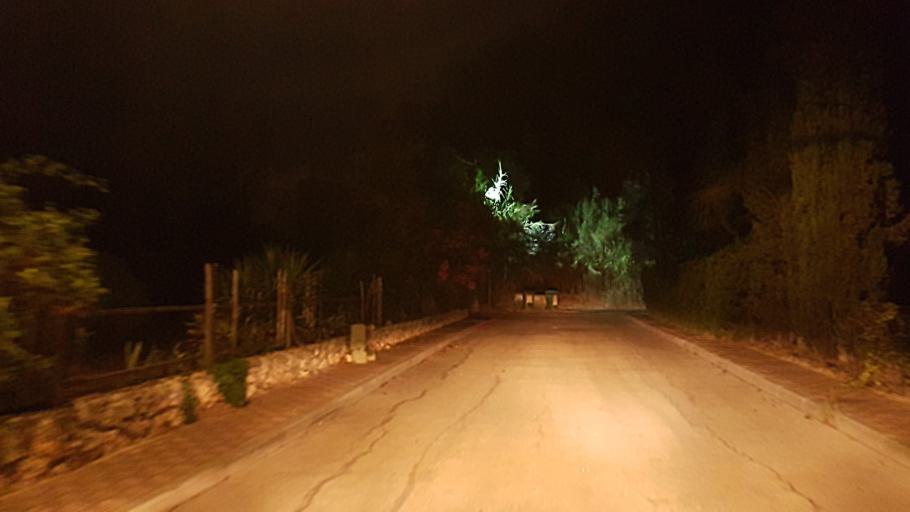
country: IL
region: Central District
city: Hod HaSharon
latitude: 32.1485
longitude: 34.8997
